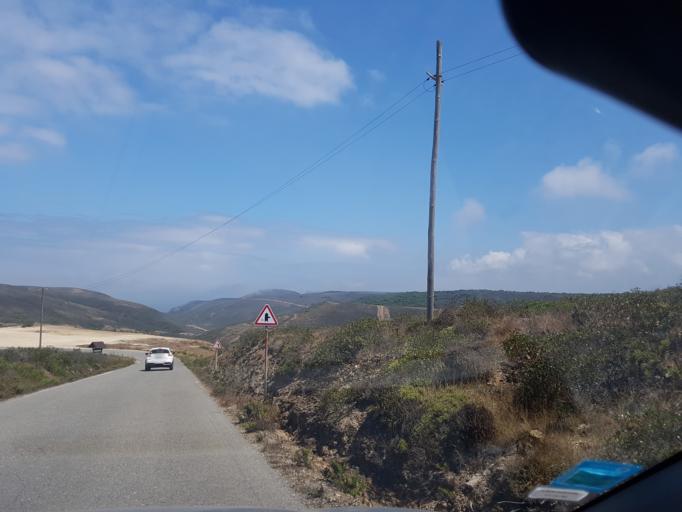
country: PT
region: Faro
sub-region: Vila do Bispo
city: Vila do Bispo
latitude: 37.0946
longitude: -8.9339
